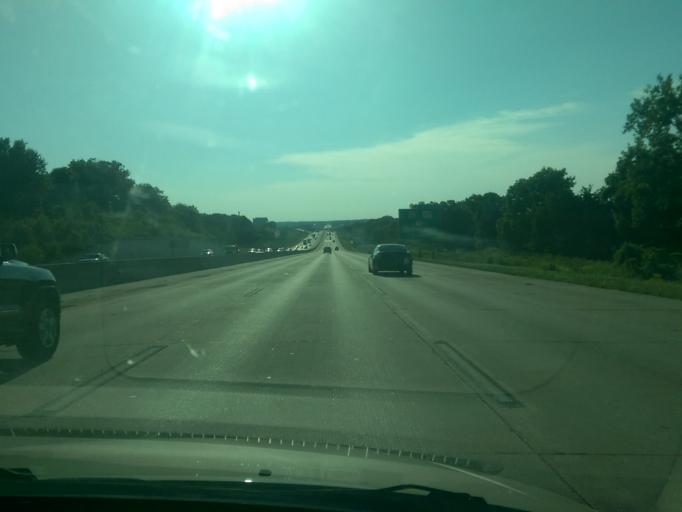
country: US
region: Missouri
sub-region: Jackson County
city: Blue Springs
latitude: 39.0364
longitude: -94.3216
